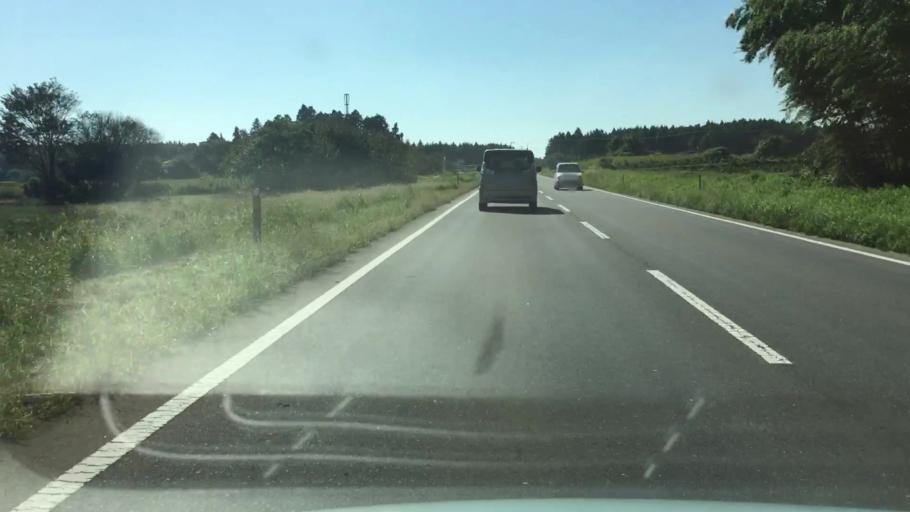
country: JP
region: Ibaraki
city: Ami
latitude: 35.9873
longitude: 140.1852
